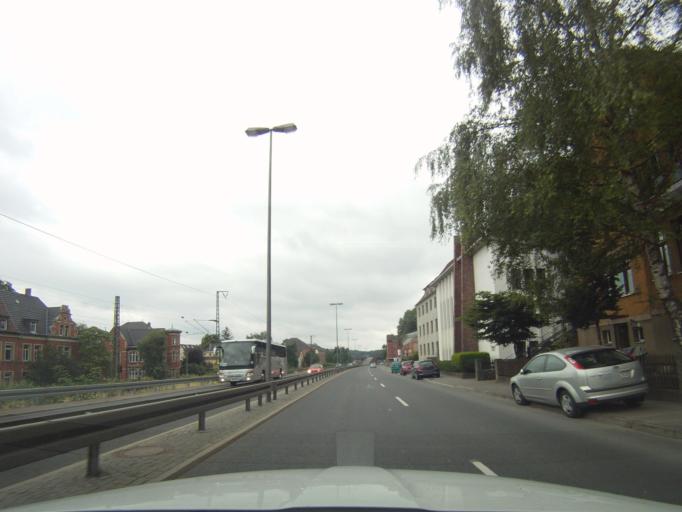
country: DE
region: Bavaria
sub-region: Upper Franconia
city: Coburg
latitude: 50.2570
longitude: 10.9579
